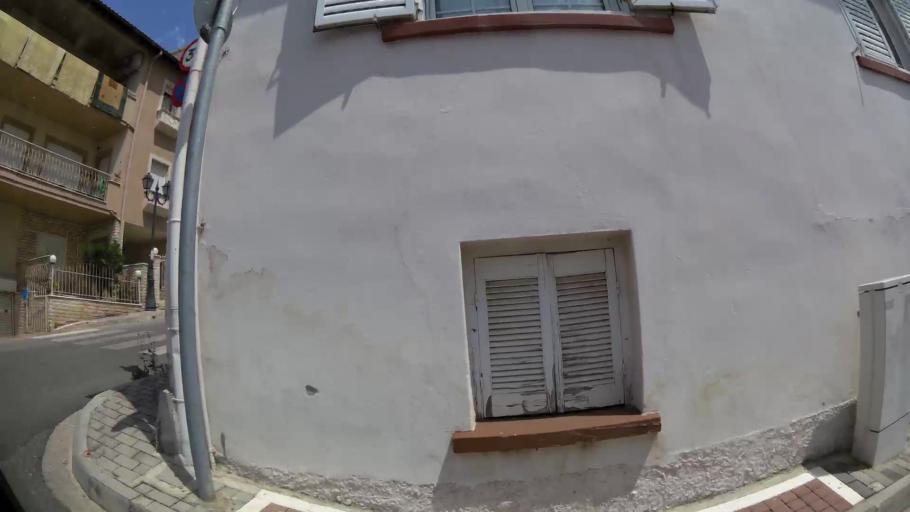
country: GR
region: West Macedonia
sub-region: Nomos Kozanis
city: Kozani
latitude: 40.3075
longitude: 21.7918
